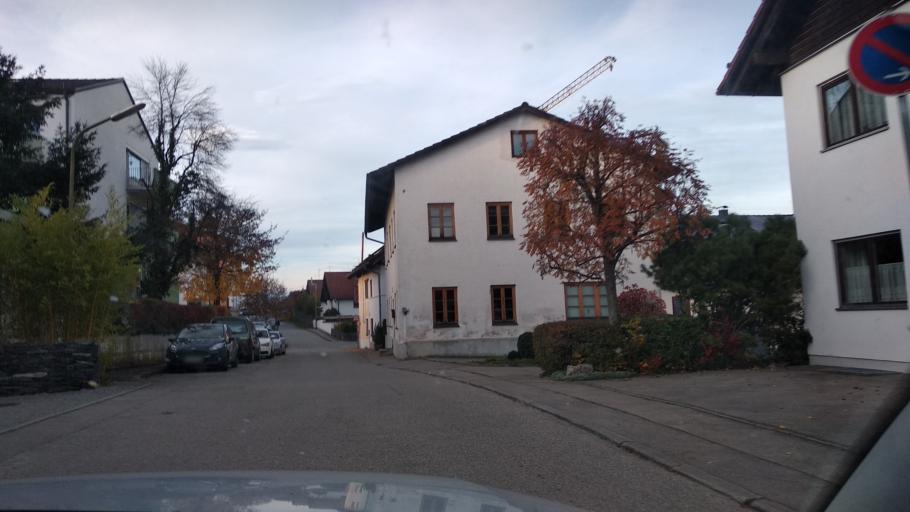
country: DE
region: Bavaria
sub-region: Upper Bavaria
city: Grafing bei Munchen
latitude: 48.0447
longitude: 11.9712
